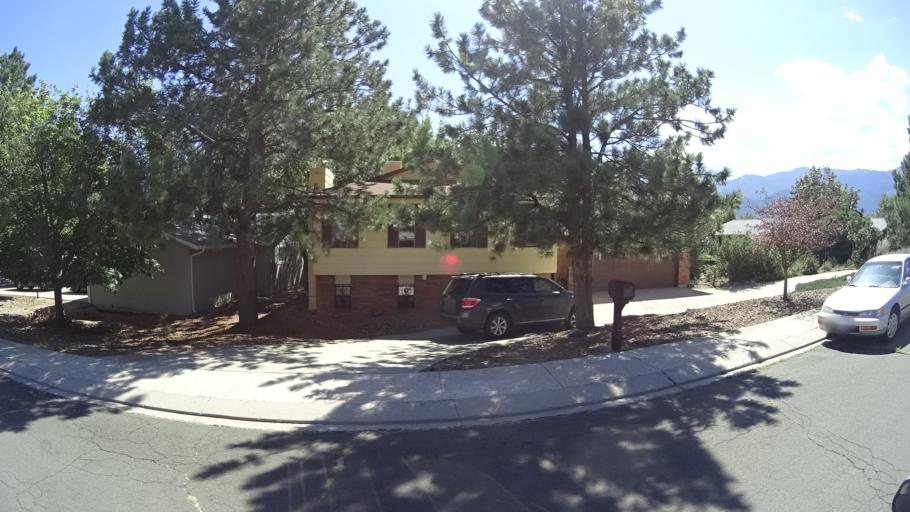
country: US
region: Colorado
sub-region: El Paso County
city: Colorado Springs
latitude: 38.8605
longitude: -104.8558
